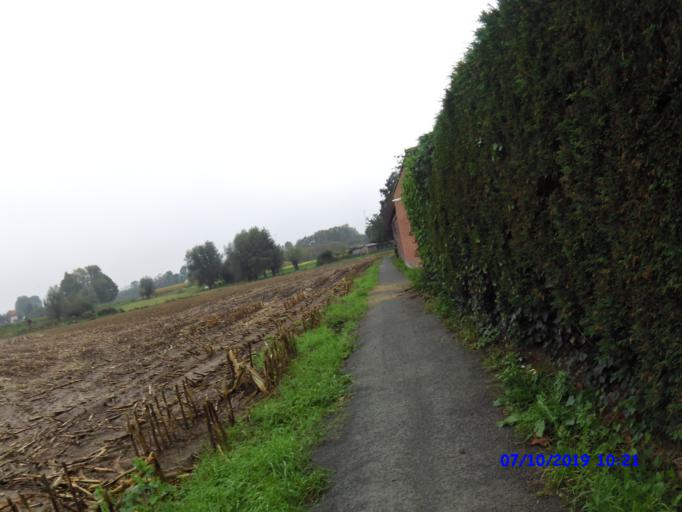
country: BE
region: Flanders
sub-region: Provincie Oost-Vlaanderen
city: Melle
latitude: 50.9930
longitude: 3.8008
